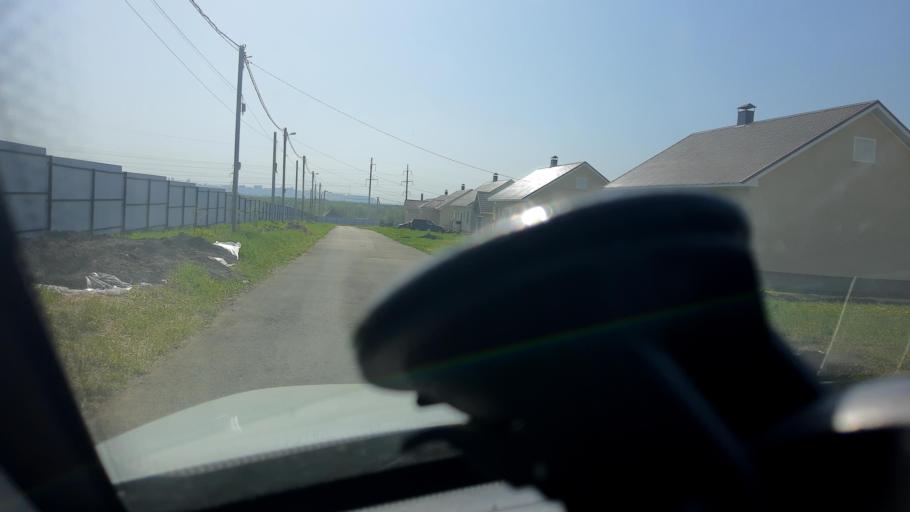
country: RU
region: Bashkortostan
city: Mikhaylovka
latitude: 54.7862
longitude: 55.8009
